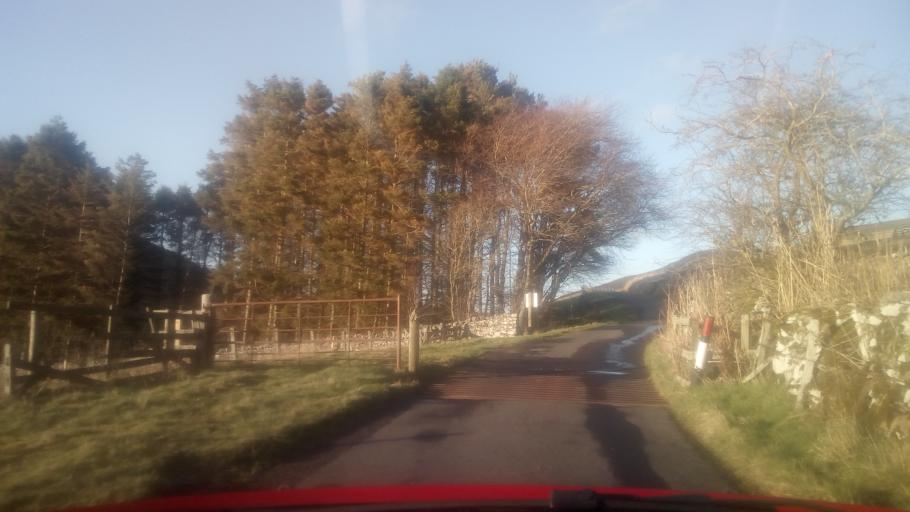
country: GB
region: Scotland
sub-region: The Scottish Borders
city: Kelso
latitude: 55.4380
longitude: -2.3636
